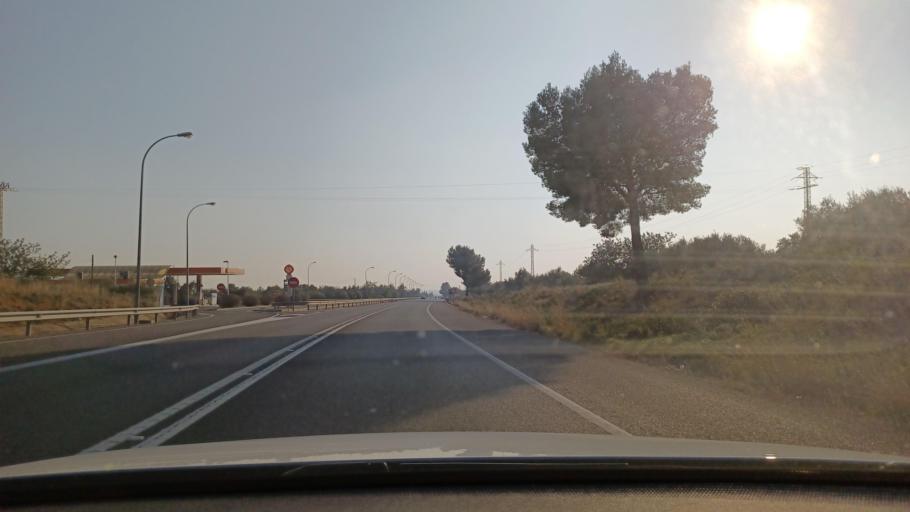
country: ES
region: Catalonia
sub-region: Provincia de Tarragona
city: L'Ampolla
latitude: 40.8384
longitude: 0.7113
